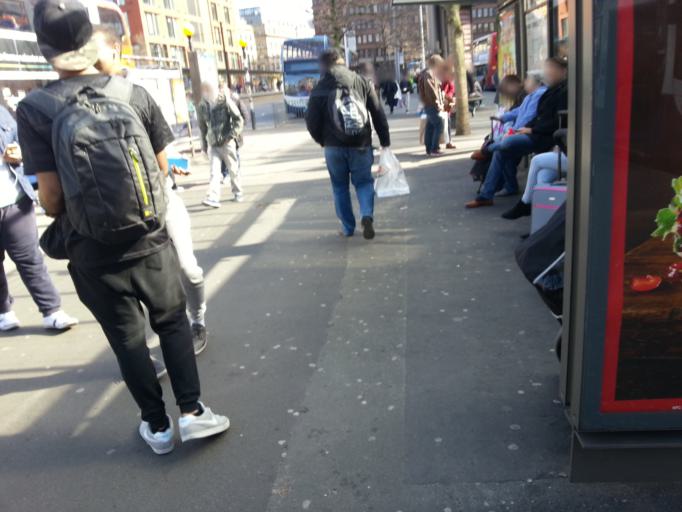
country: GB
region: England
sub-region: Manchester
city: Manchester
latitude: 53.4806
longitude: -2.2381
